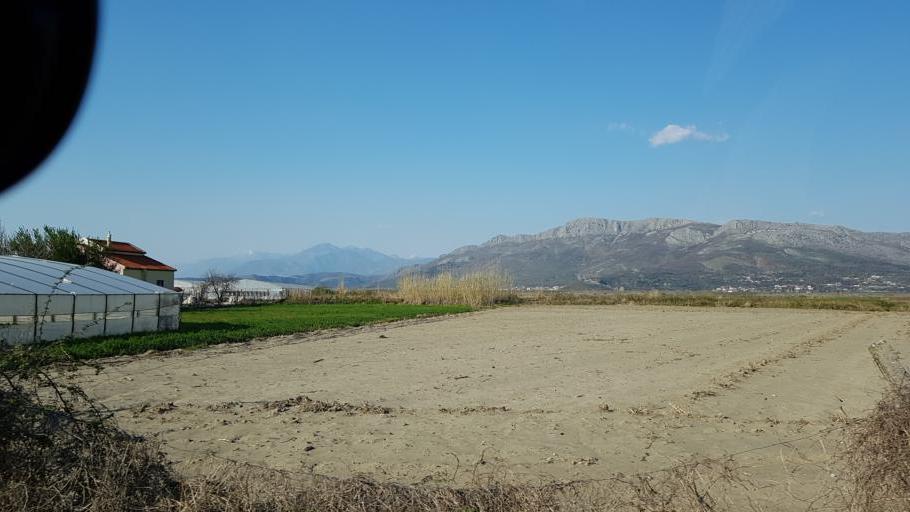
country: AL
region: Shkoder
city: Vukatane
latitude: 41.9921
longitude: 19.5636
